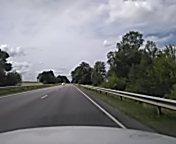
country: LT
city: Virbalis
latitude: 54.6338
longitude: 22.9074
